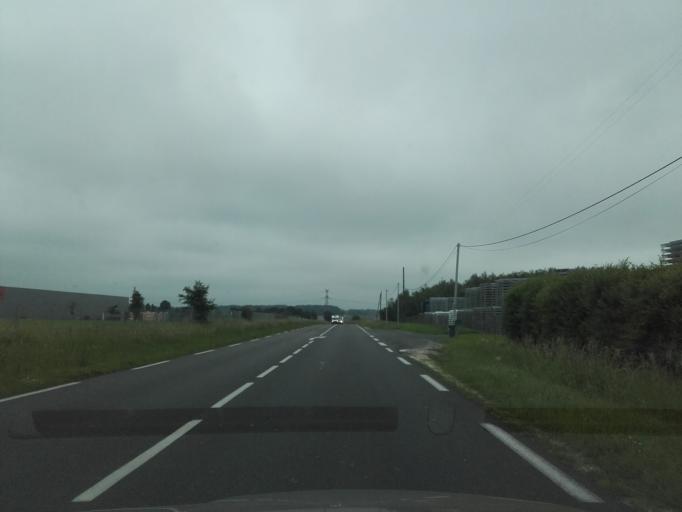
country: FR
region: Centre
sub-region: Departement d'Indre-et-Loire
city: Parcay-Meslay
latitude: 47.4699
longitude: 0.7517
